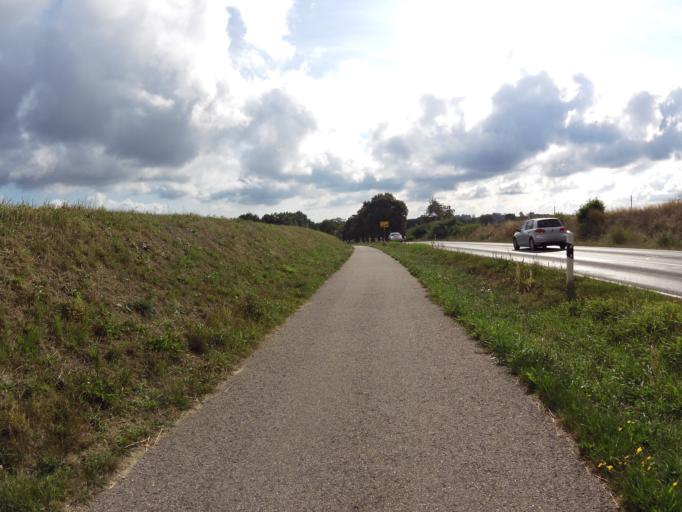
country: DE
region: Mecklenburg-Vorpommern
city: Seebad Bansin
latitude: 53.9669
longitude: 14.0655
